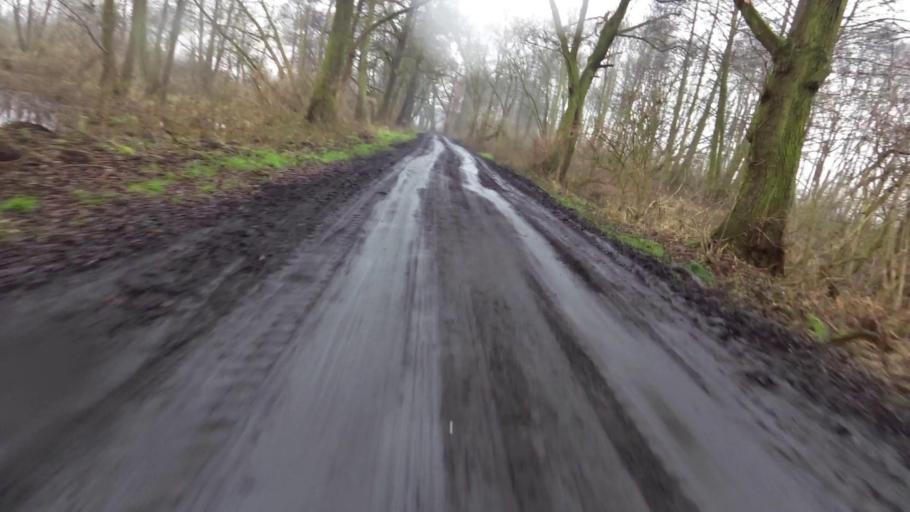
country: PL
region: West Pomeranian Voivodeship
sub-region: Szczecin
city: Szczecin
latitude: 53.4402
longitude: 14.7179
